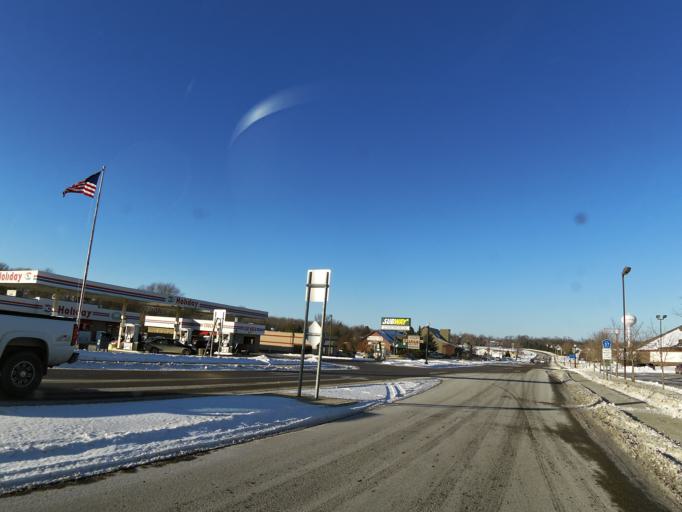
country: US
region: Minnesota
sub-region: Le Sueur County
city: New Prague
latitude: 44.5438
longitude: -93.5614
